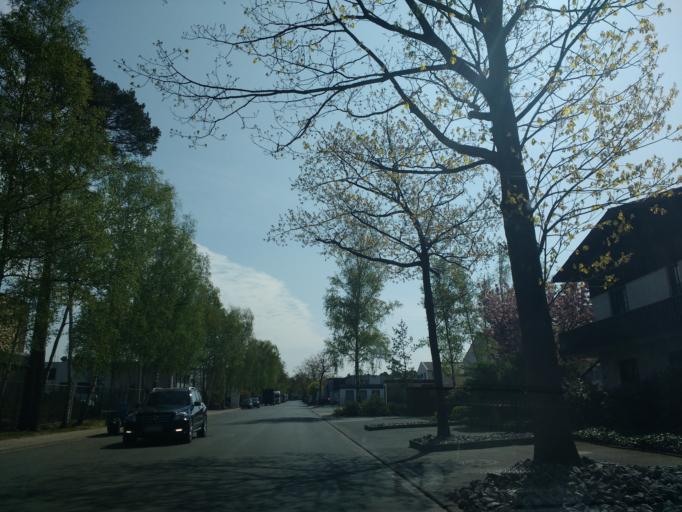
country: DE
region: North Rhine-Westphalia
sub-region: Regierungsbezirk Detmold
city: Hovelhof
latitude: 51.8318
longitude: 8.6485
